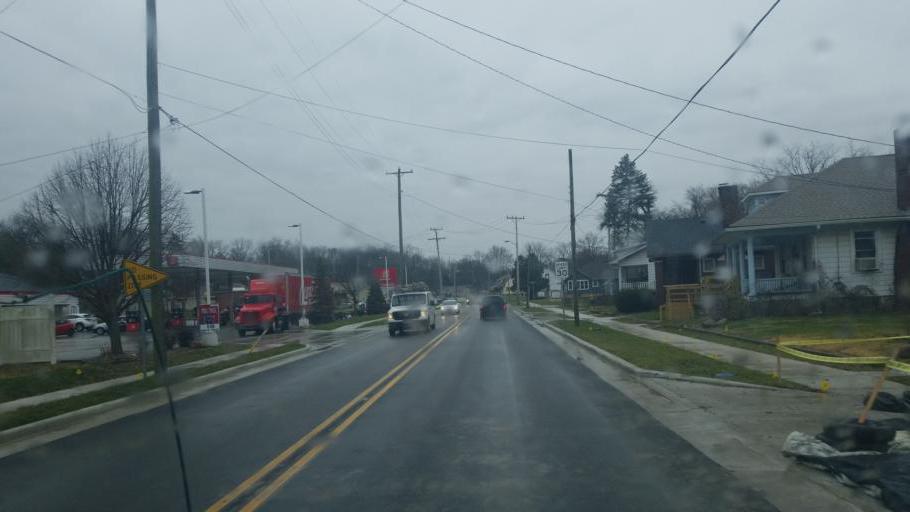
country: US
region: Indiana
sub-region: Shelby County
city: Shelbyville
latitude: 39.5123
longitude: -85.7742
